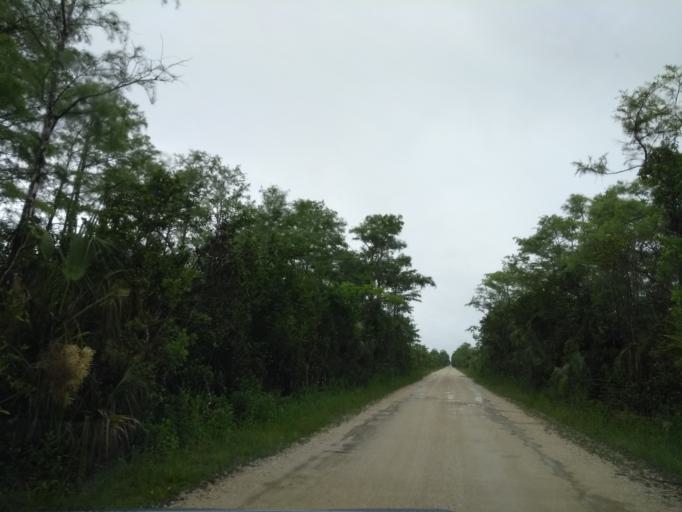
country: US
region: Florida
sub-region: Miami-Dade County
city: The Hammocks
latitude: 25.7602
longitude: -81.0324
